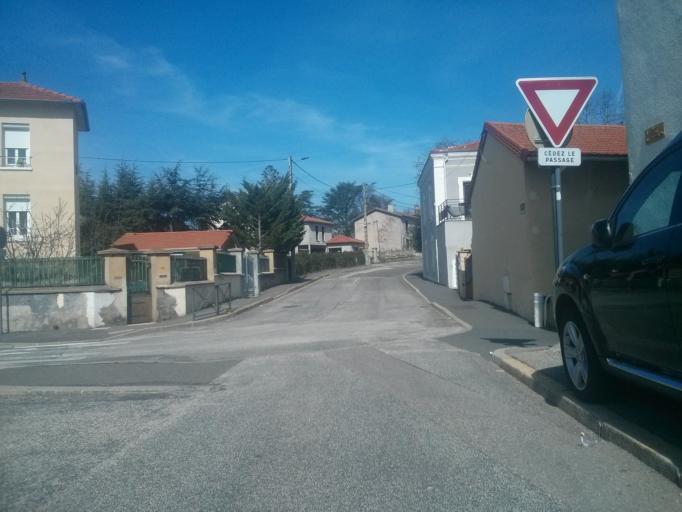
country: FR
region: Rhone-Alpes
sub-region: Departement de la Loire
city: Saint-Etienne
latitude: 45.4257
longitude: 4.4217
